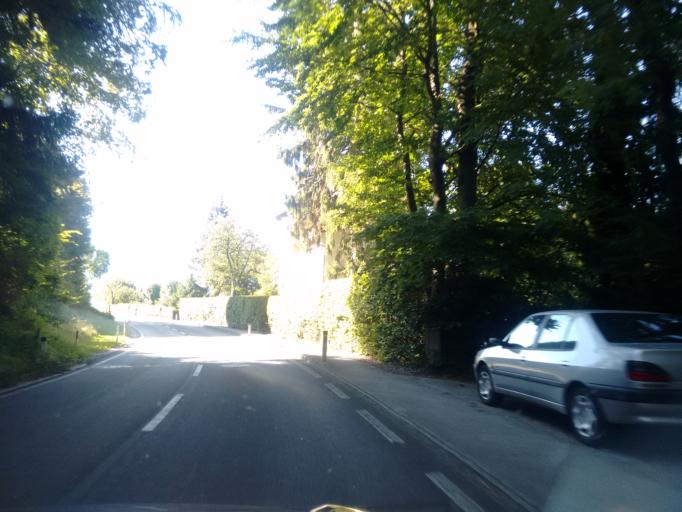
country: AT
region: Upper Austria
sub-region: Politischer Bezirk Vocklabruck
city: Attersee
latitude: 47.8905
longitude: 13.5680
